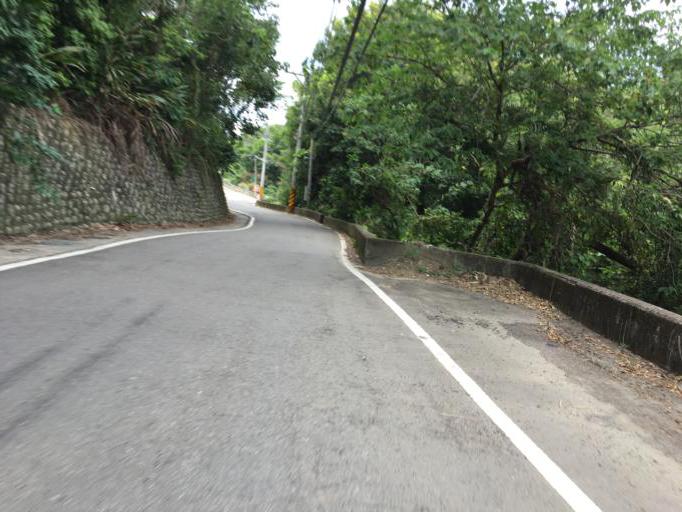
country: TW
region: Taiwan
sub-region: Hsinchu
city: Hsinchu
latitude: 24.6997
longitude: 120.9612
